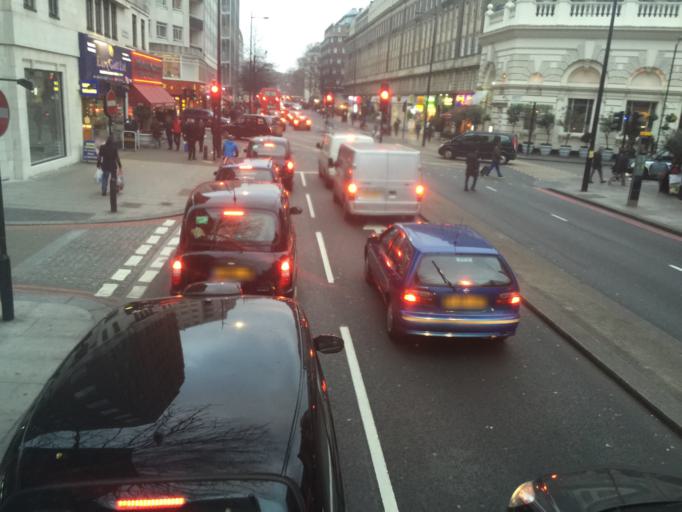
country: GB
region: England
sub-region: Greater London
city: Bayswater
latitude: 51.5153
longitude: -0.1632
